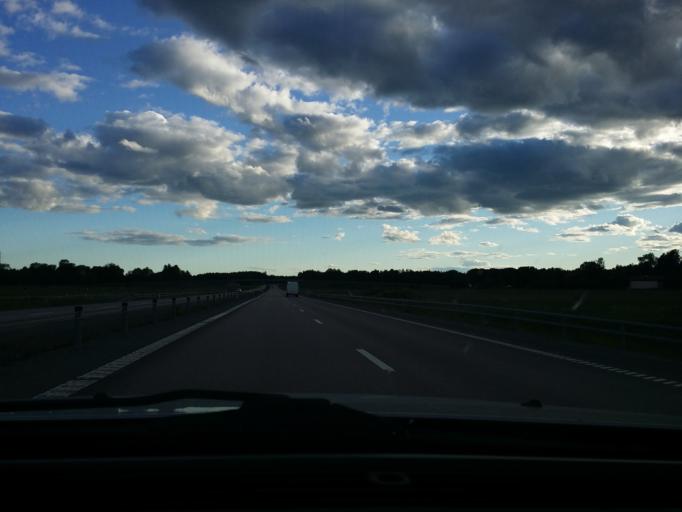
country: SE
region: Uppsala
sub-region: Enkopings Kommun
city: Hummelsta
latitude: 59.6467
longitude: 16.9729
